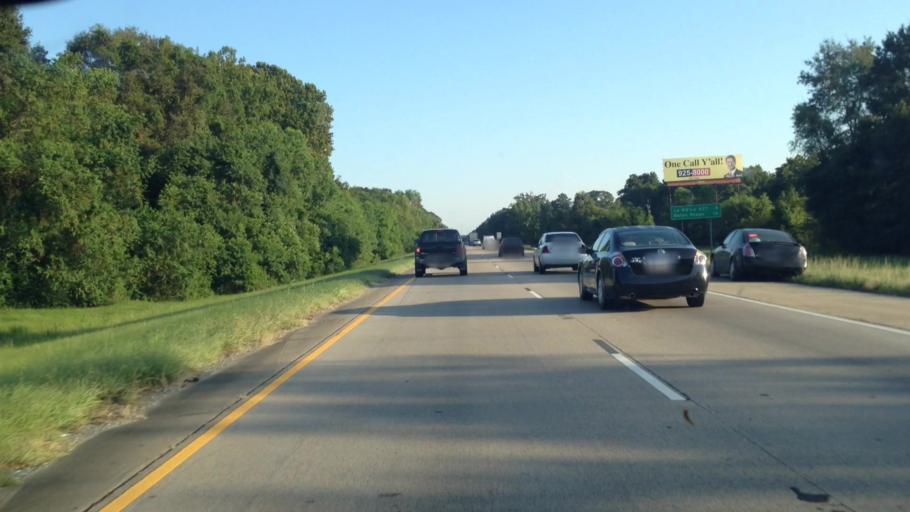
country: US
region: Louisiana
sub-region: Ascension Parish
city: Prairieville
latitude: 30.2825
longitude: -90.9890
